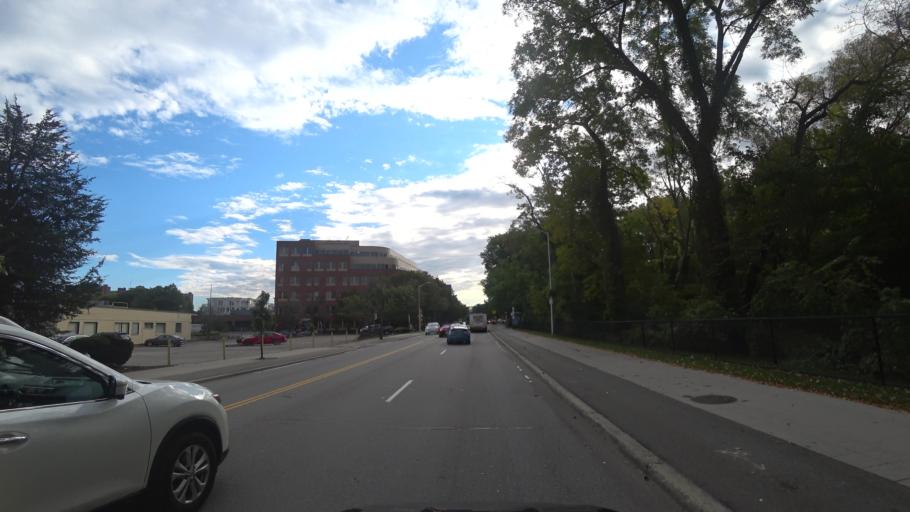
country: US
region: Massachusetts
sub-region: Middlesex County
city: Arlington
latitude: 42.3894
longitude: -71.1473
